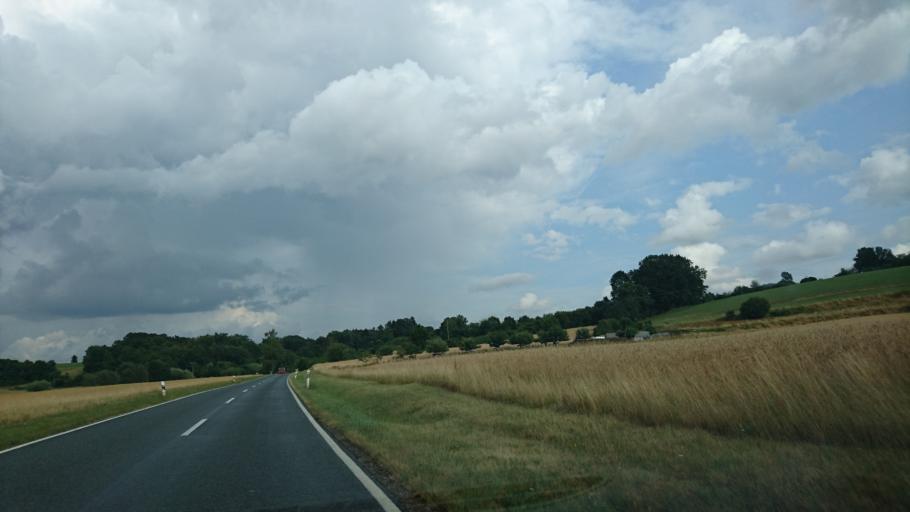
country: DE
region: Bavaria
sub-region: Regierungsbezirk Mittelfranken
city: Heideck
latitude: 49.1317
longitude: 11.1351
